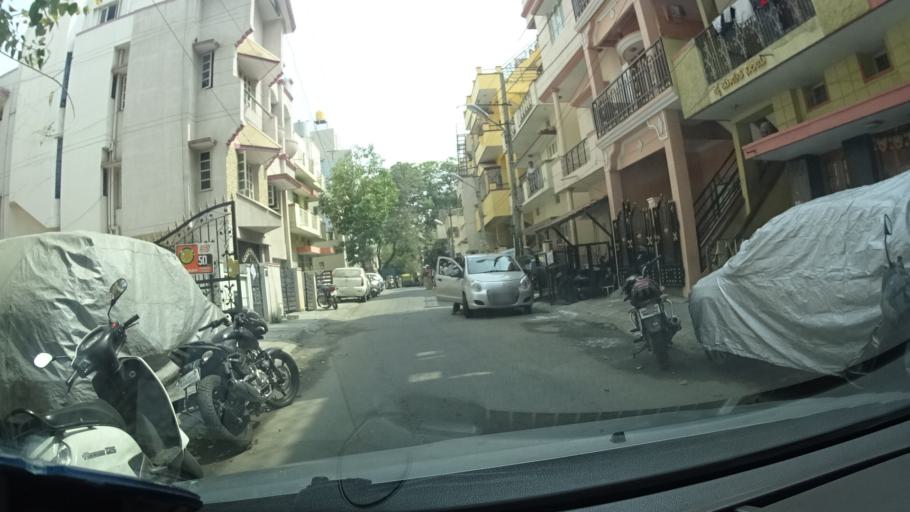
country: IN
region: Karnataka
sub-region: Bangalore Urban
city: Bangalore
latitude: 12.9996
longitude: 77.5594
